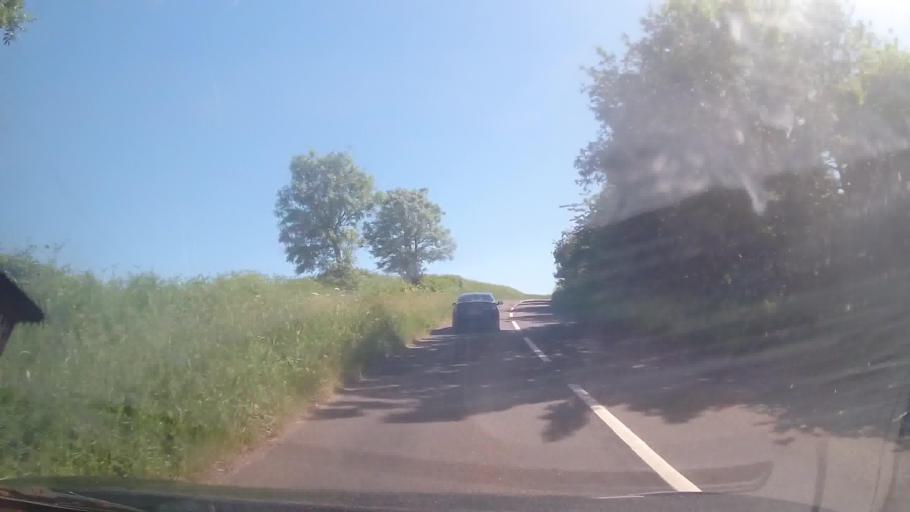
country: GB
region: England
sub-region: Borough of Torbay
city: Brixham
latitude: 50.3883
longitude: -3.5563
